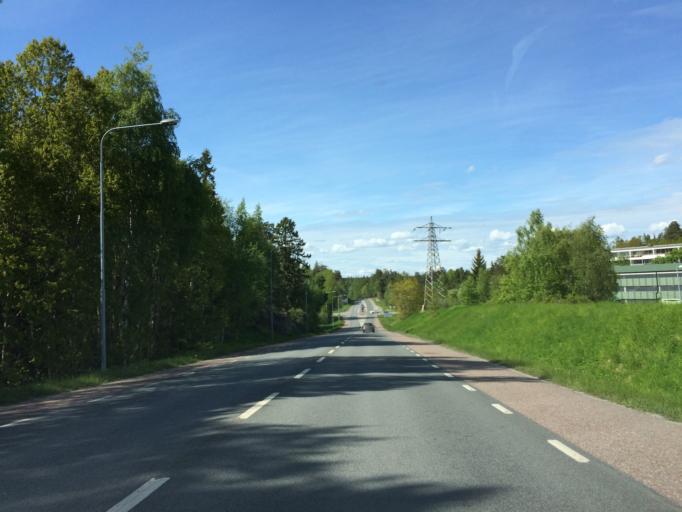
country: SE
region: Stockholm
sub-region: Sollentuna Kommun
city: Sollentuna
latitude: 59.4315
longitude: 17.9937
